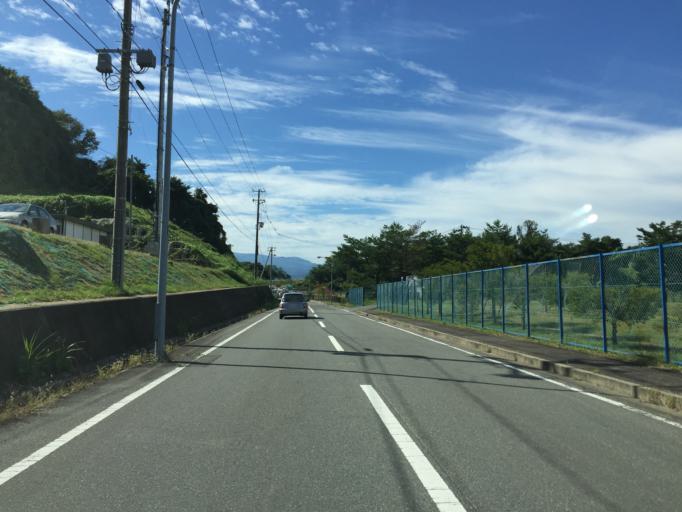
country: JP
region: Fukushima
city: Hobaramachi
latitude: 37.7852
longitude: 140.5175
